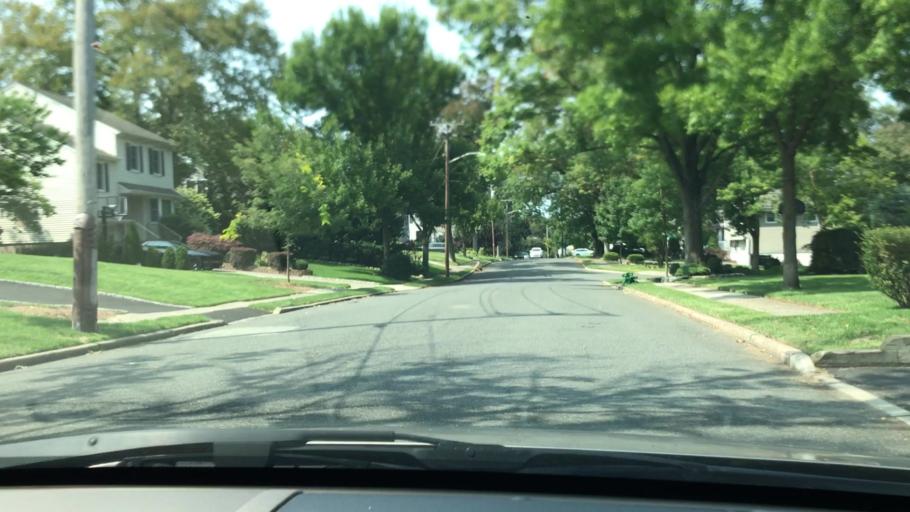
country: US
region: New Jersey
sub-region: Bergen County
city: Oradell
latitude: 40.9497
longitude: -74.0542
